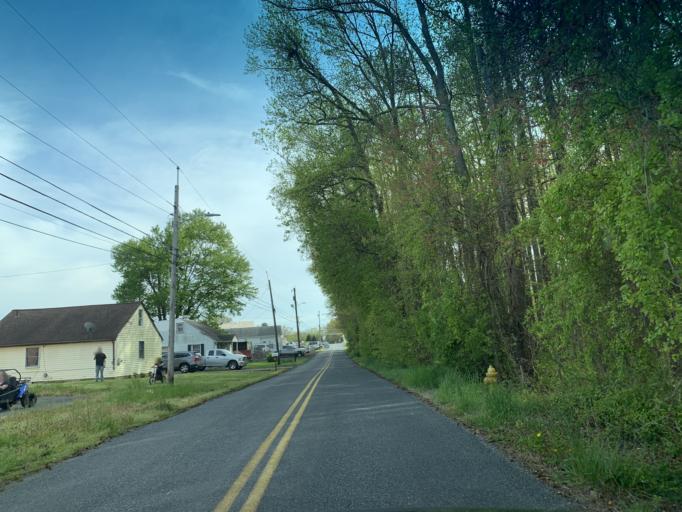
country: US
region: Maryland
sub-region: Harford County
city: Perryman
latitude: 39.4879
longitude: -76.2036
